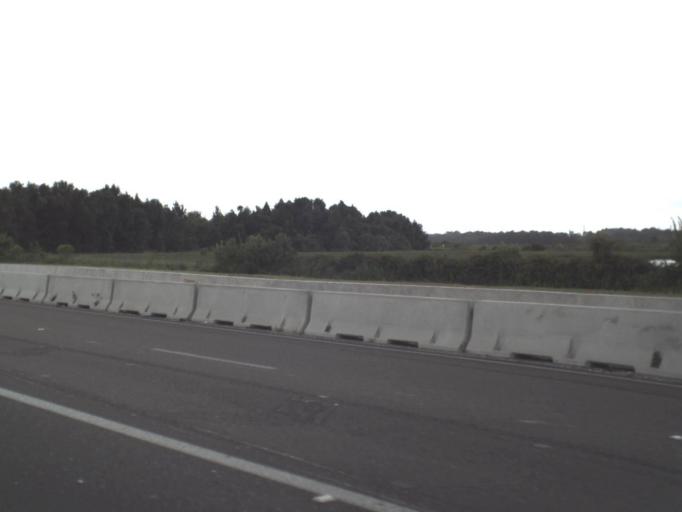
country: US
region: Florida
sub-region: Hillsborough County
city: Pebble Creek
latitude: 28.1900
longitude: -82.3860
